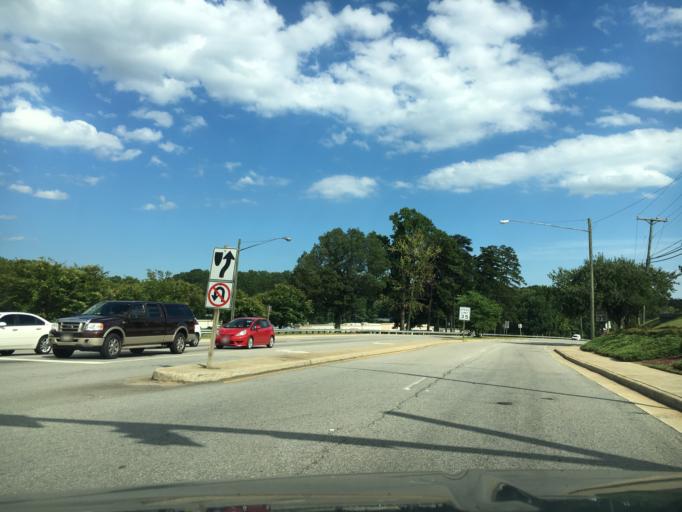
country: US
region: Virginia
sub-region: Halifax County
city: South Boston
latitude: 36.7146
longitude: -78.9143
